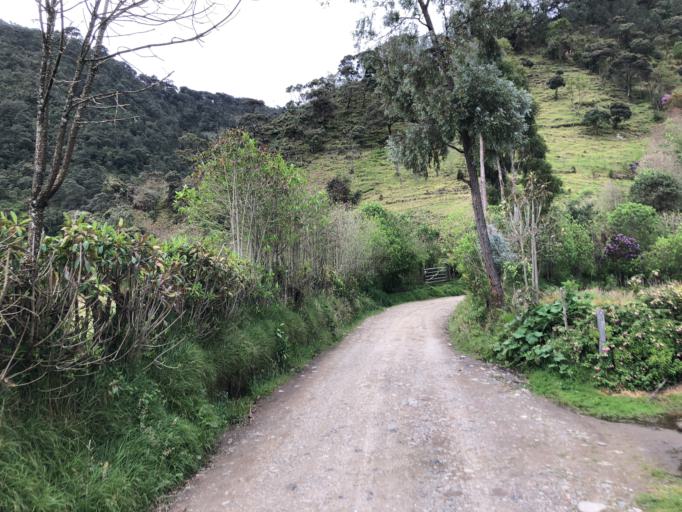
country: CO
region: Cauca
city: Totoro
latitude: 2.5069
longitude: -76.3607
